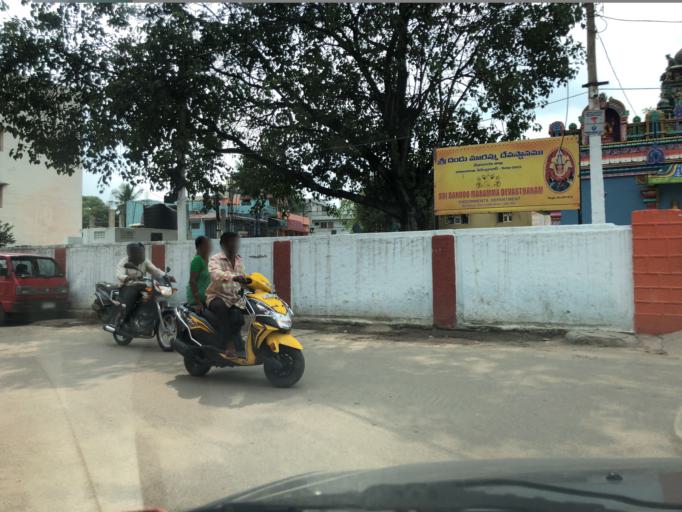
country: IN
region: Telangana
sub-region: Hyderabad
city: Malkajgiri
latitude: 17.4466
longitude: 78.4837
